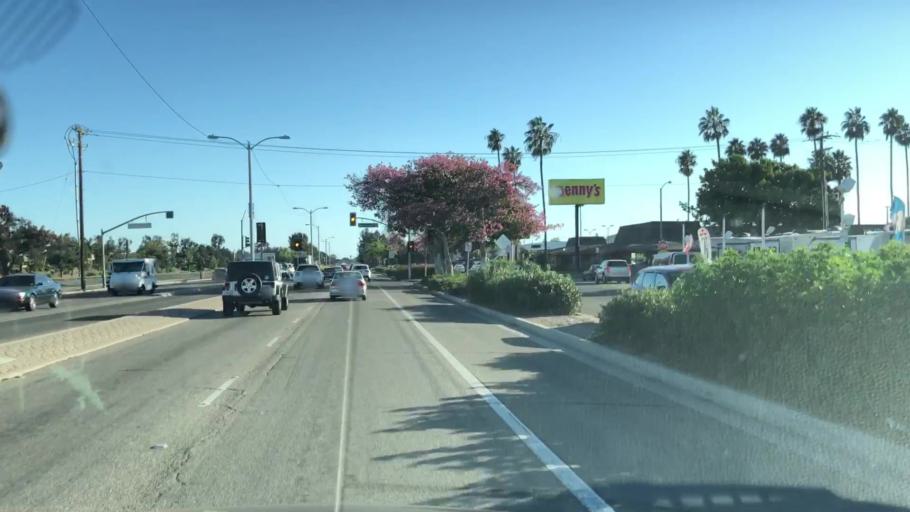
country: US
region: California
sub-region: Ventura County
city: Oxnard
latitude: 34.2150
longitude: -119.1773
